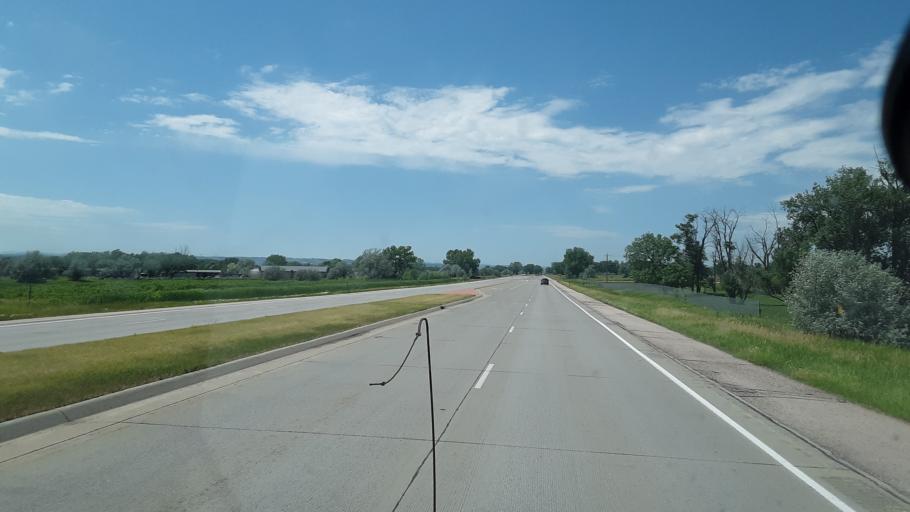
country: US
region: South Dakota
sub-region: Pennington County
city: Rapid Valley
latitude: 44.0372
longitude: -103.1075
